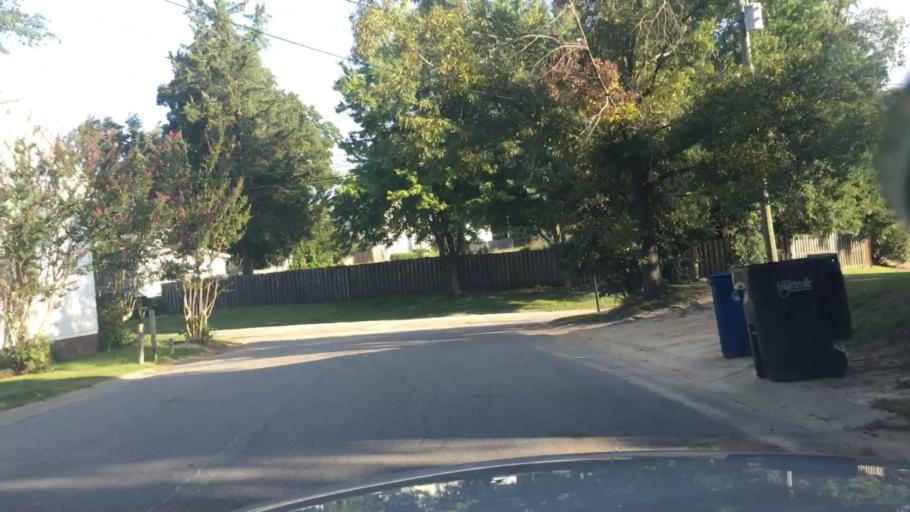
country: US
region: North Carolina
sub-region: Cumberland County
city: Fayetteville
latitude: 35.0499
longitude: -78.8927
